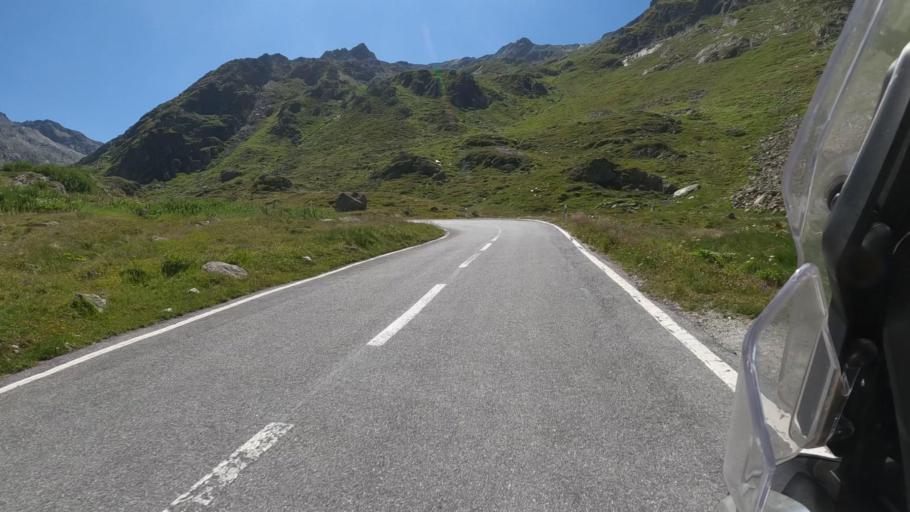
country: IT
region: Aosta Valley
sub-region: Valle d'Aosta
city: San Leonardo
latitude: 45.8808
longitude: 7.1832
